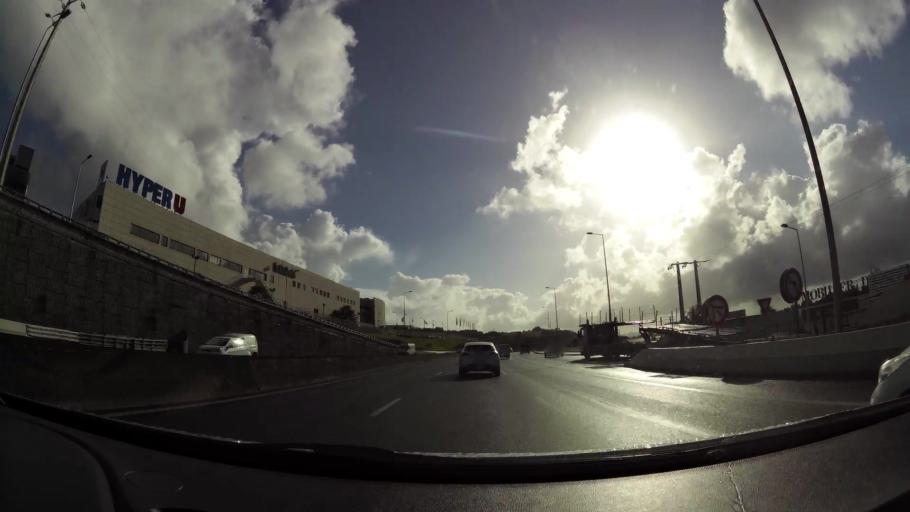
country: MQ
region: Martinique
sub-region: Martinique
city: Le Lamentin
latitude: 14.6184
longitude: -61.0207
